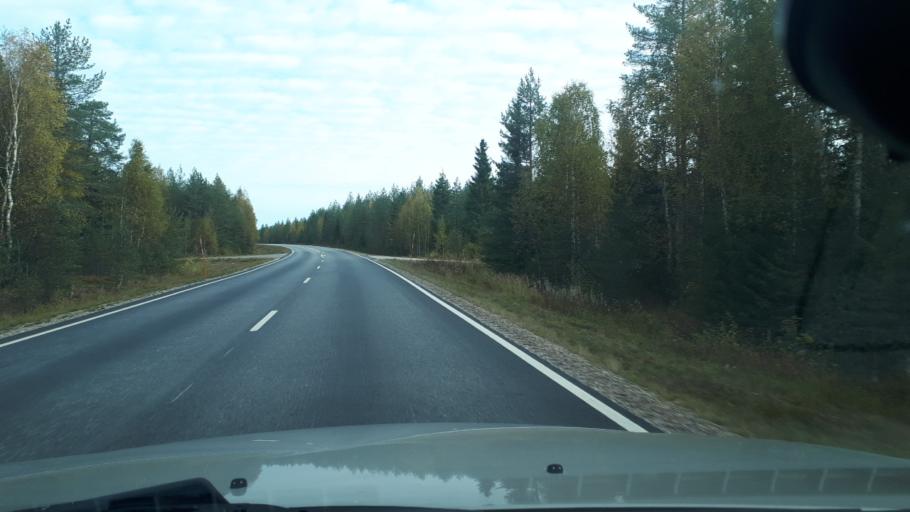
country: FI
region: Northern Ostrobothnia
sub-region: Oulu
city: Yli-Ii
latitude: 65.9017
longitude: 25.7321
